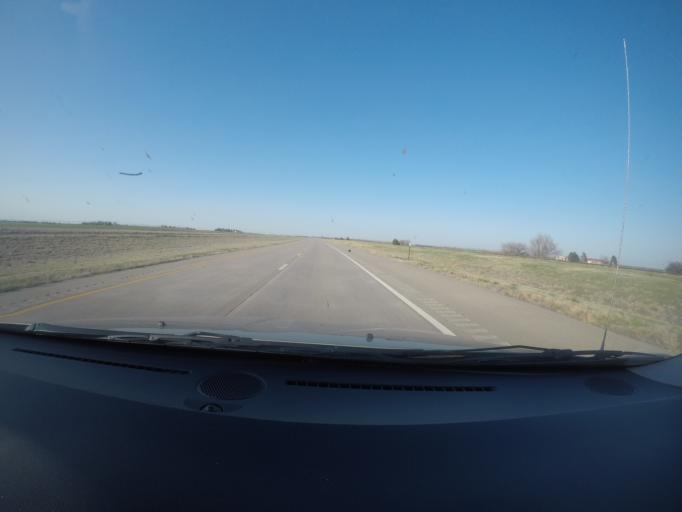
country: US
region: Kansas
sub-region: McPherson County
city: Inman
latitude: 38.2974
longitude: -97.7261
